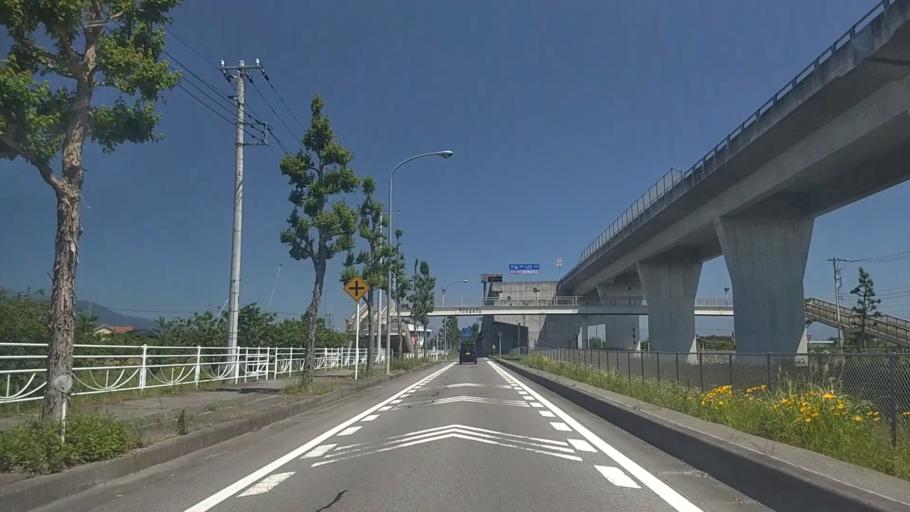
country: JP
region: Yamanashi
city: Ryuo
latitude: 35.6107
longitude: 138.4807
